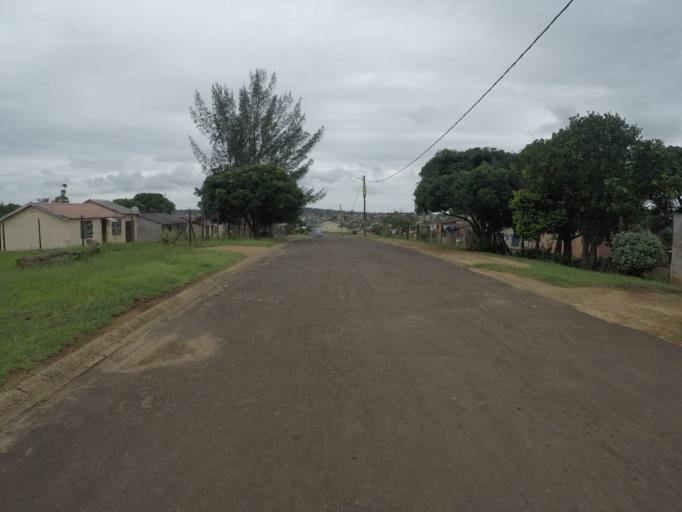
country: ZA
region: KwaZulu-Natal
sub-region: uThungulu District Municipality
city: Empangeni
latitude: -28.7690
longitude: 31.8703
